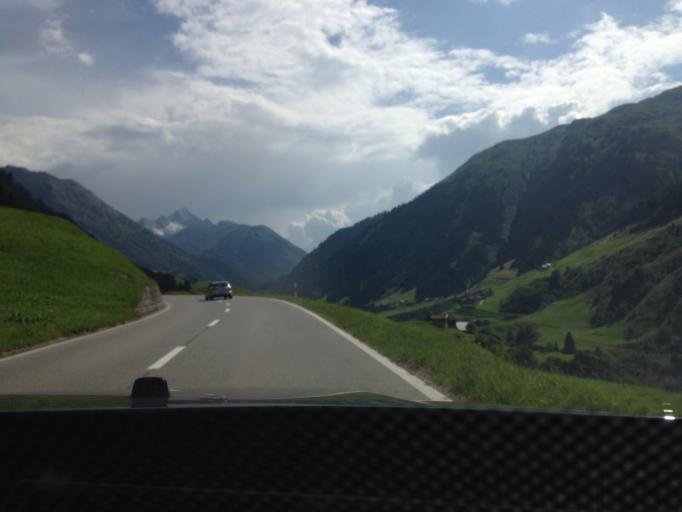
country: CH
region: Grisons
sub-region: Surselva District
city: Disentis
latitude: 46.6650
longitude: 8.8579
